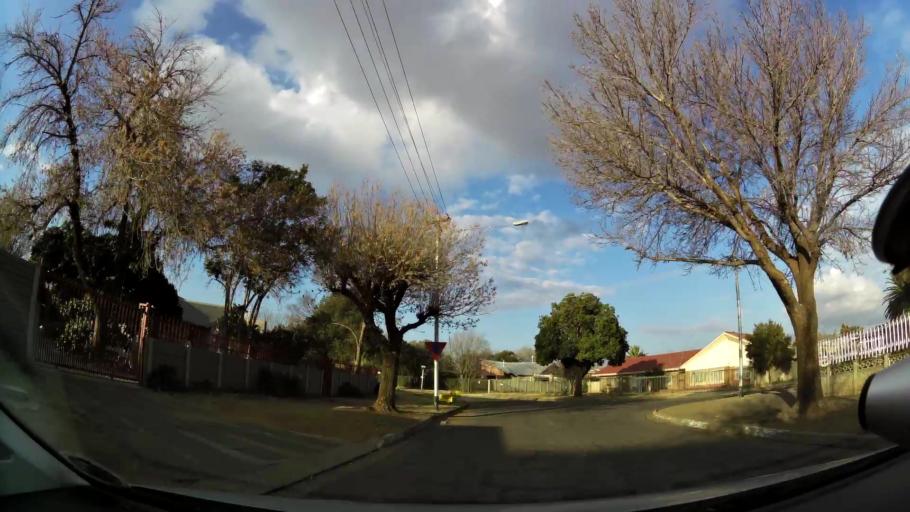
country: ZA
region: Orange Free State
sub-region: Mangaung Metropolitan Municipality
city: Bloemfontein
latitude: -29.1421
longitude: 26.1949
